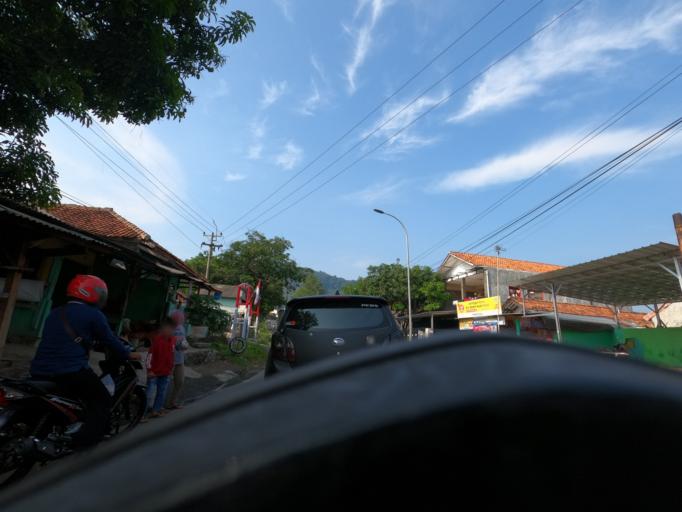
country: ID
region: West Java
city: Lembang
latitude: -6.6253
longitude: 107.7232
